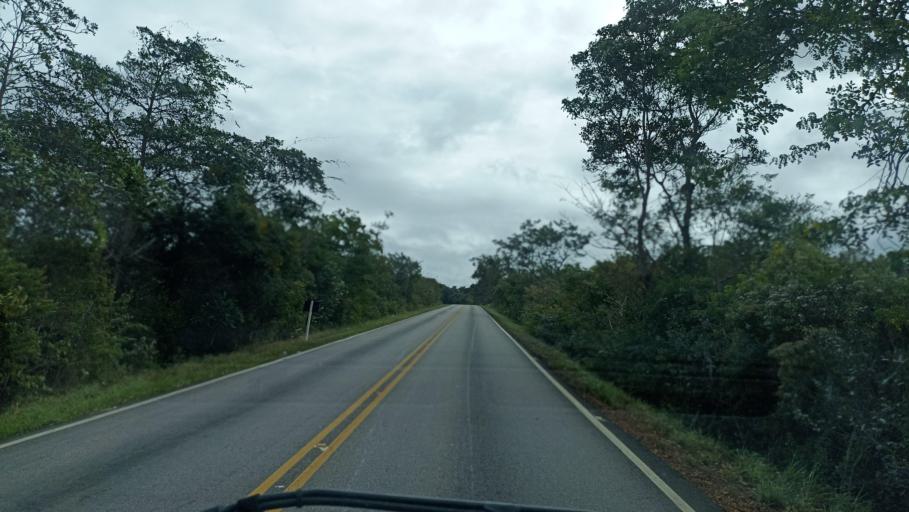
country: BR
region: Bahia
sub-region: Andarai
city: Vera Cruz
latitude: -12.9302
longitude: -41.2456
